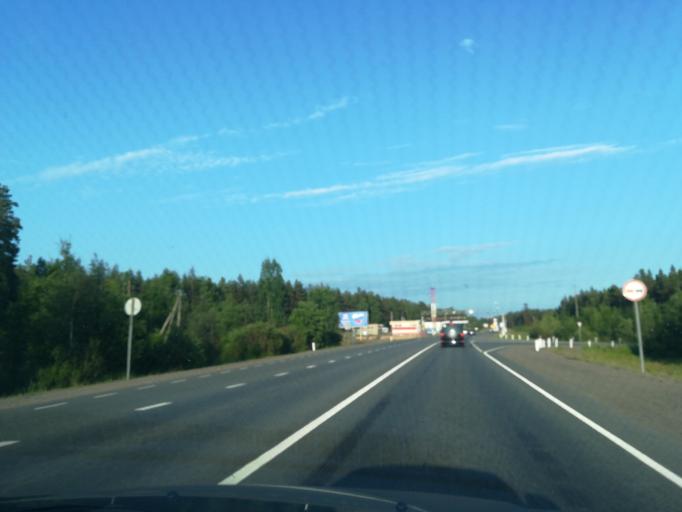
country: RU
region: Leningrad
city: Vyborg
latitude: 60.6652
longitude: 28.9267
